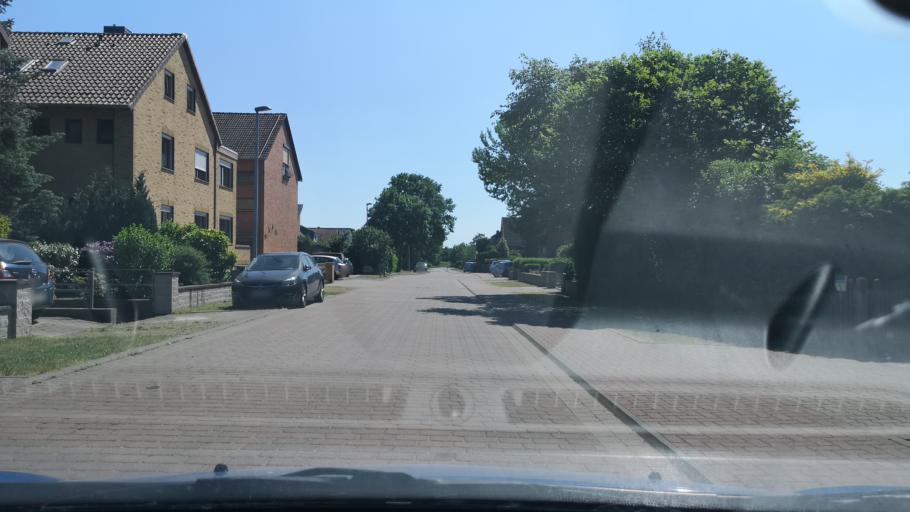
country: DE
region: Lower Saxony
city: Garbsen
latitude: 52.4554
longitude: 9.5616
